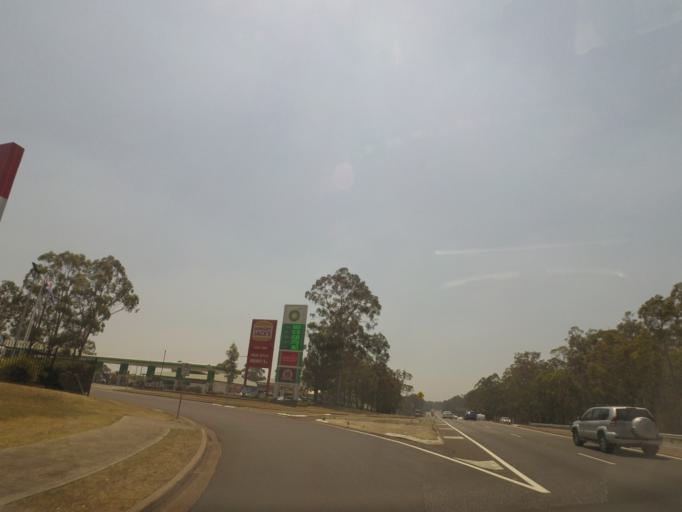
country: AU
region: New South Wales
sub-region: Newcastle
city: Beresfield
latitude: -32.8124
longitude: 151.6388
